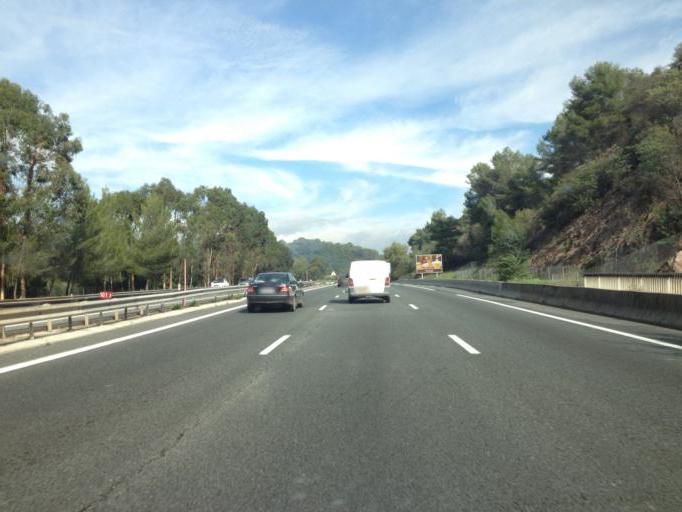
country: FR
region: Provence-Alpes-Cote d'Azur
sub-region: Departement des Alpes-Maritimes
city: La Roquette-sur-Siagne
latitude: 43.5654
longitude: 6.9733
